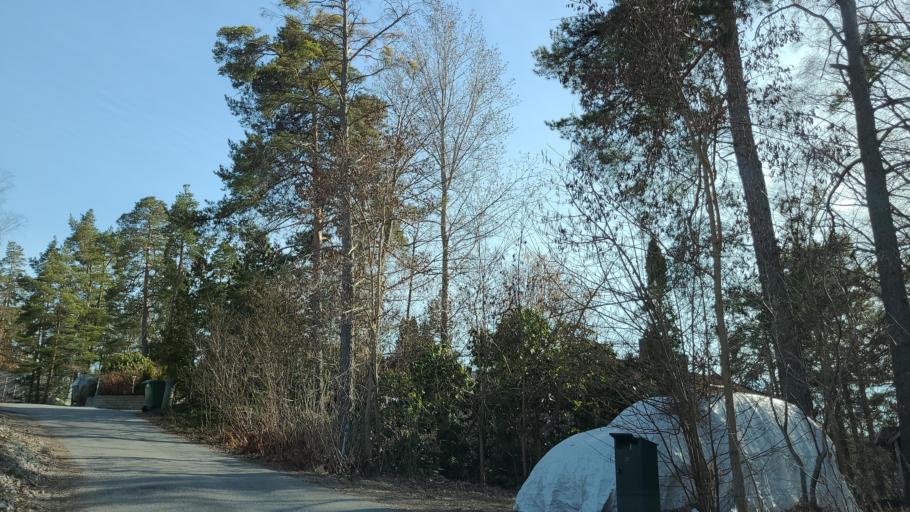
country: SE
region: Stockholm
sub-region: Ekero Kommun
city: Ekeroe
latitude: 59.2906
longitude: 17.7567
